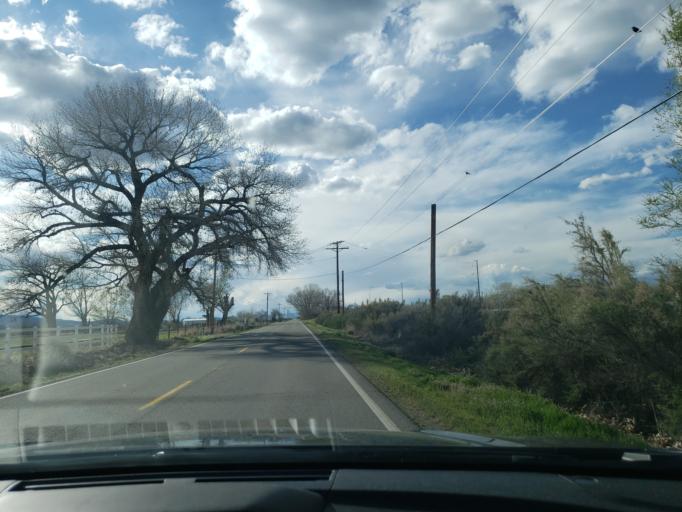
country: US
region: Colorado
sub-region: Mesa County
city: Redlands
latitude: 39.1223
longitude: -108.6701
